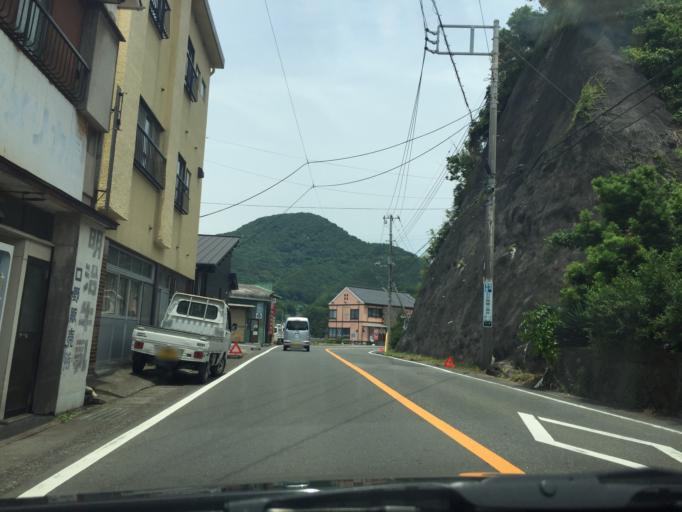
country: JP
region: Shizuoka
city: Numazu
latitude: 35.0443
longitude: 138.9015
